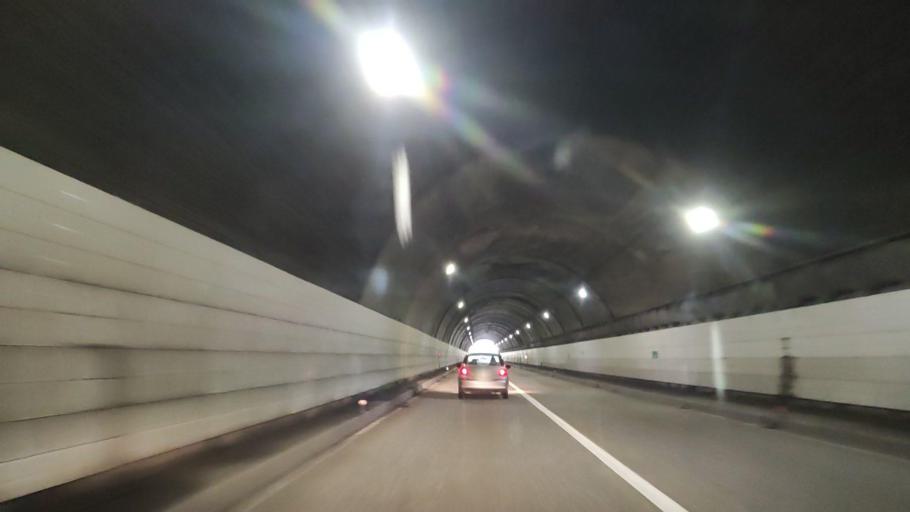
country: JP
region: Akita
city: Takanosu
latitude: 40.2179
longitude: 140.2360
